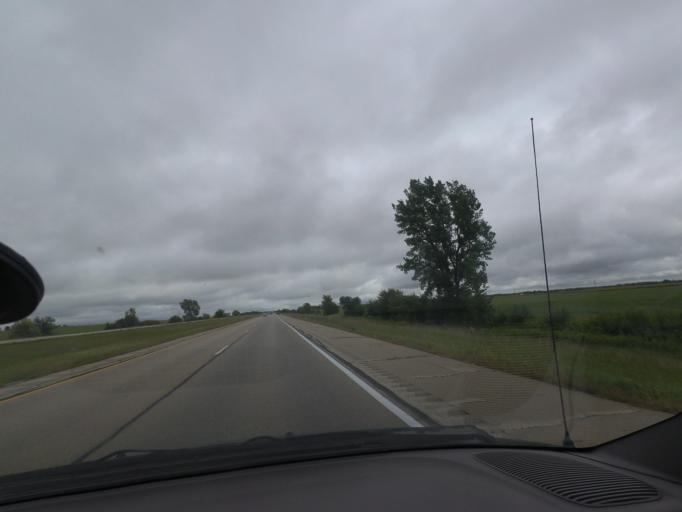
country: US
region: Illinois
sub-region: Piatt County
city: Monticello
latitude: 40.0208
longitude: -88.7050
